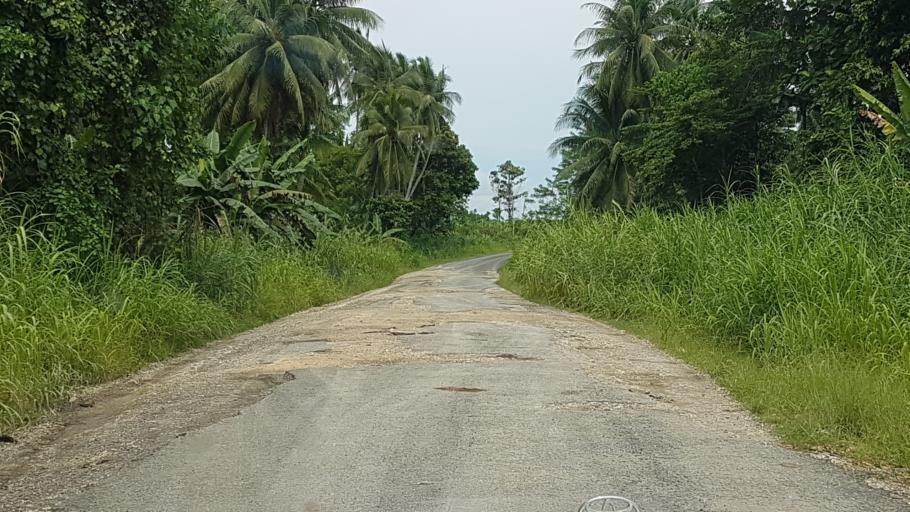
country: PG
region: Madang
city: Madang
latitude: -4.7297
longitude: 145.6453
